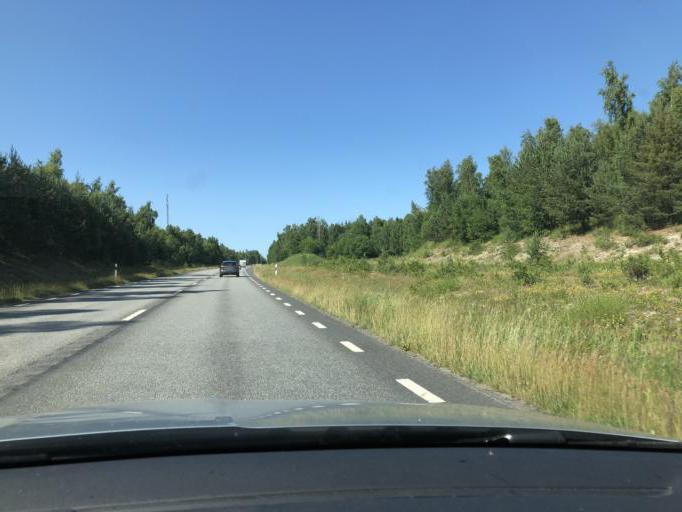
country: SE
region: Skane
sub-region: Bromolla Kommun
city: Bromoella
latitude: 56.0681
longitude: 14.4989
